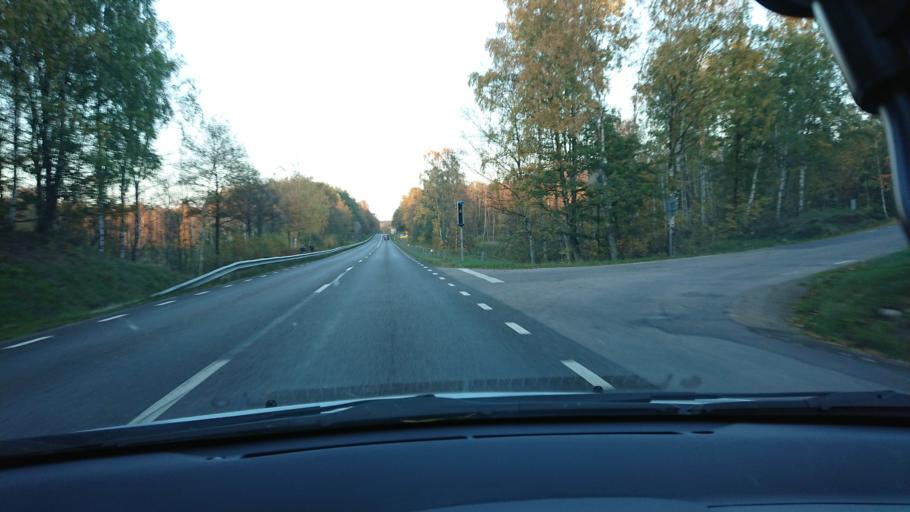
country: SE
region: Halland
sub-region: Halmstads Kommun
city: Aled
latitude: 56.7017
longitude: 13.0176
